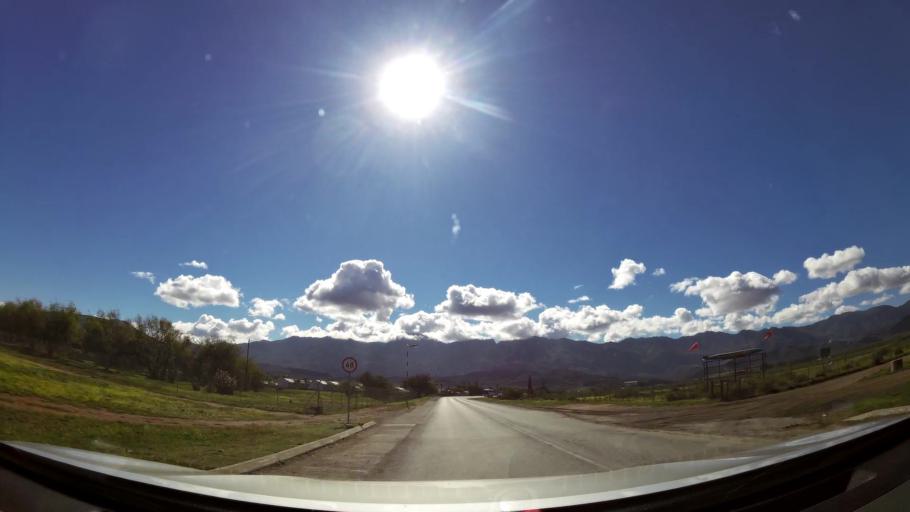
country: ZA
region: Western Cape
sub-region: Cape Winelands District Municipality
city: Ashton
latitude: -33.8133
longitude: 19.8976
